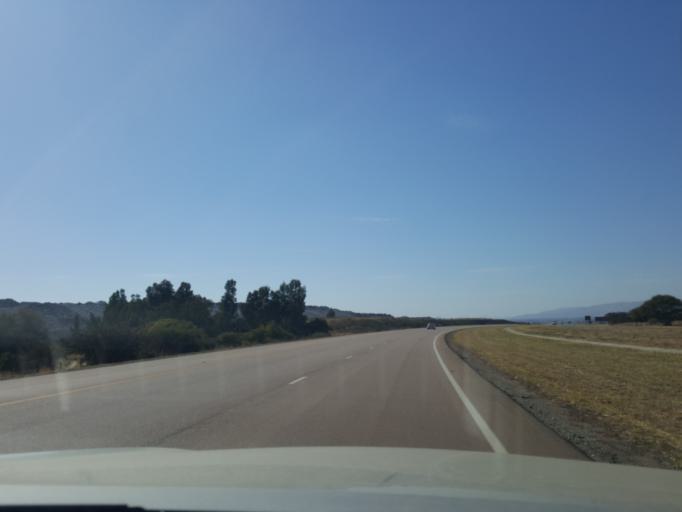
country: ZA
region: North-West
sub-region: Bojanala Platinum District Municipality
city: Rustenburg
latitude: -25.7469
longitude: 27.5099
